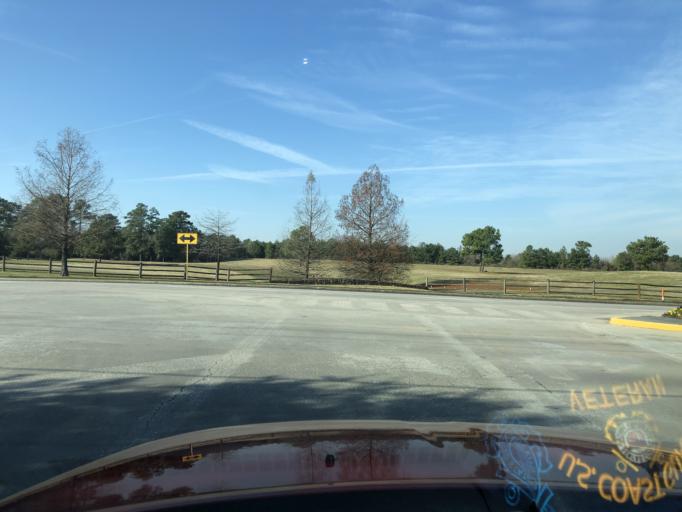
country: US
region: Texas
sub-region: Harris County
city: Tomball
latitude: 30.0402
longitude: -95.5627
